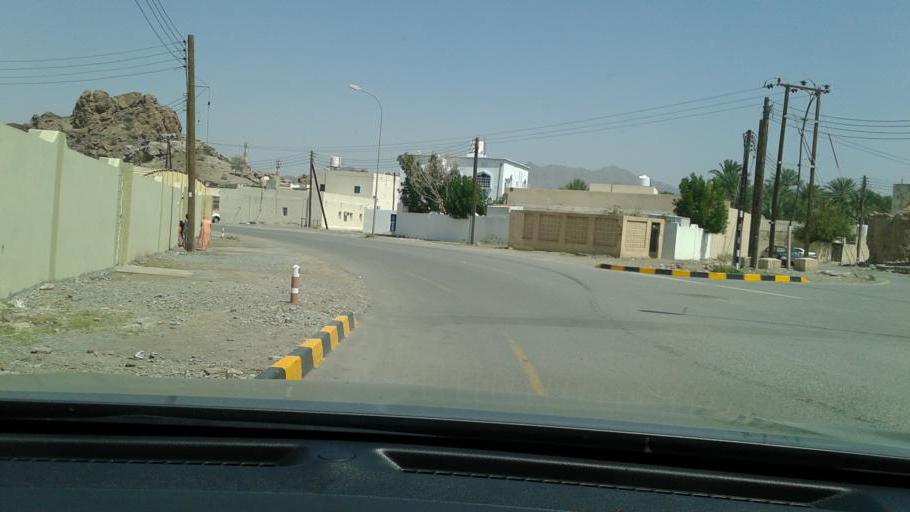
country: OM
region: Al Batinah
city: Rustaq
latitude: 23.3936
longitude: 57.4117
